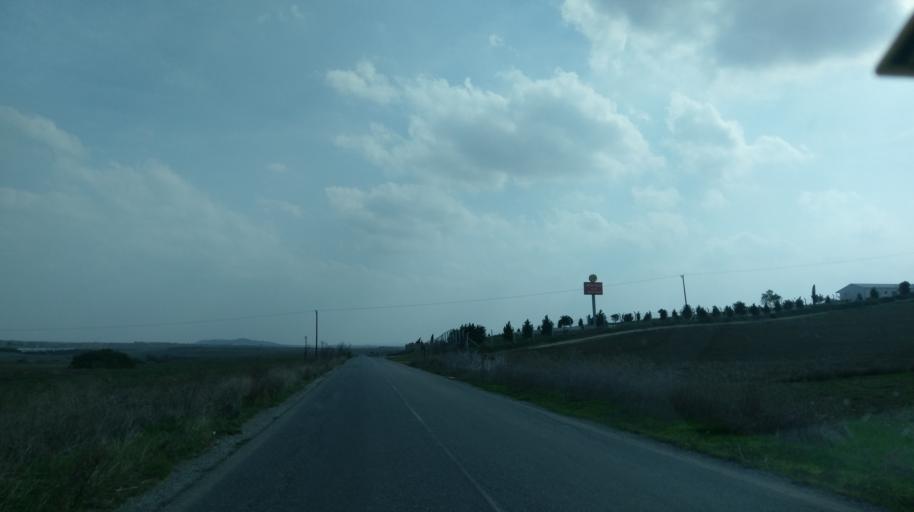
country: CY
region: Keryneia
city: Lapithos
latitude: 35.2537
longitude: 33.1435
